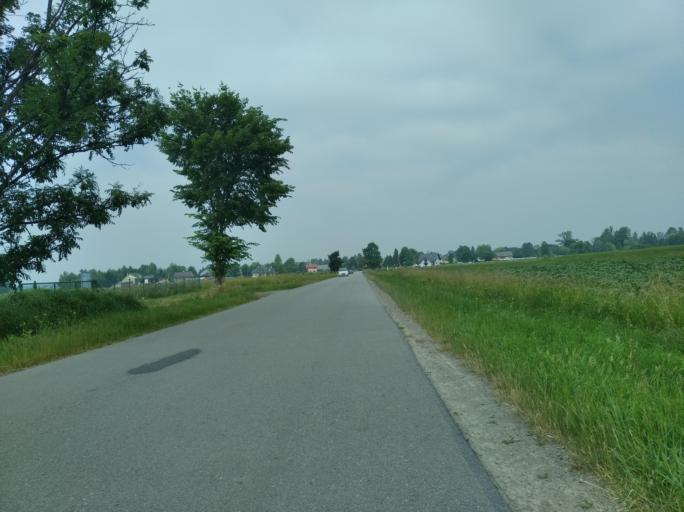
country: PL
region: Subcarpathian Voivodeship
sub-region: Powiat sanocki
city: Besko
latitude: 49.6136
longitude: 21.9494
